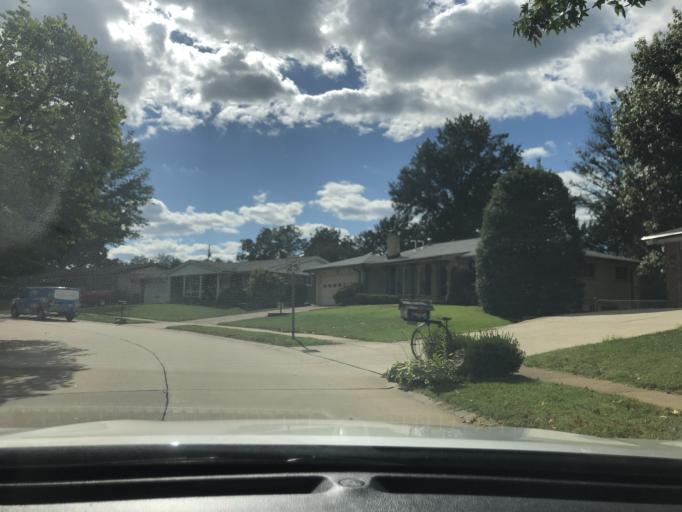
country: US
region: Missouri
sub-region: Saint Louis County
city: Concord
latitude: 38.5013
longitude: -90.3571
